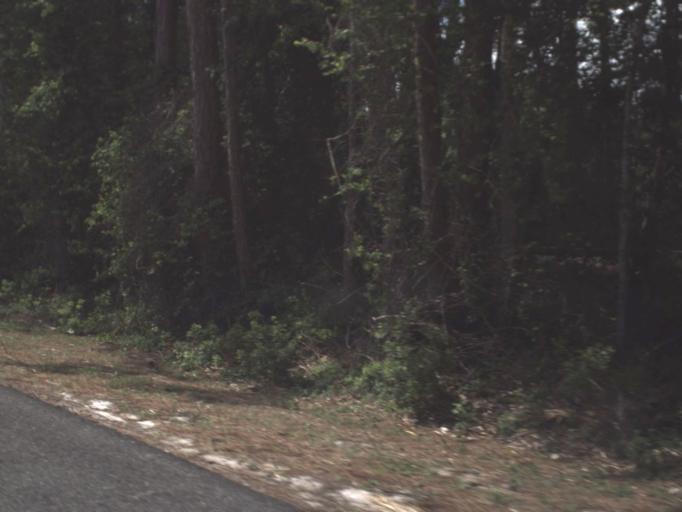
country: US
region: Florida
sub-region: Flagler County
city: Bunnell
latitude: 29.4398
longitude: -81.2366
